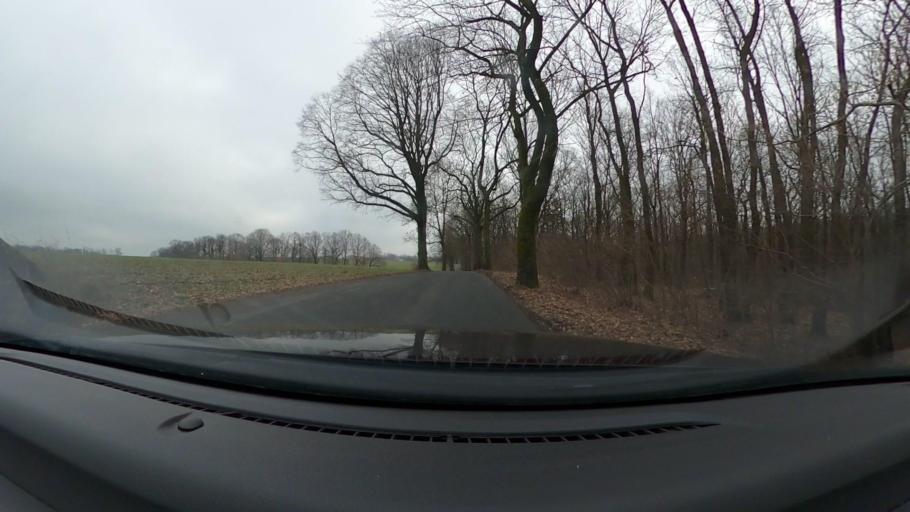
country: DE
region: Saxony
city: Oberschona
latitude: 50.9165
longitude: 13.2575
